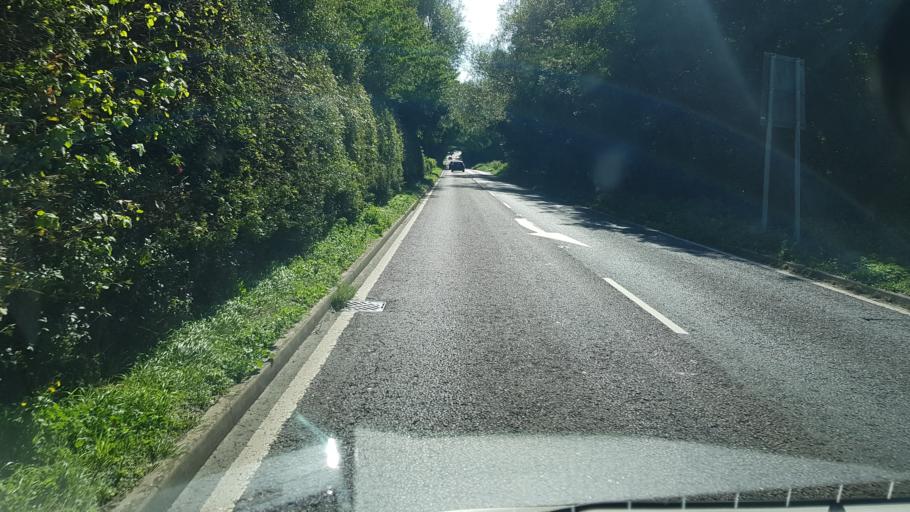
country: GB
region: England
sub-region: Kent
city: Kings Hill
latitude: 51.2550
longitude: 0.3704
